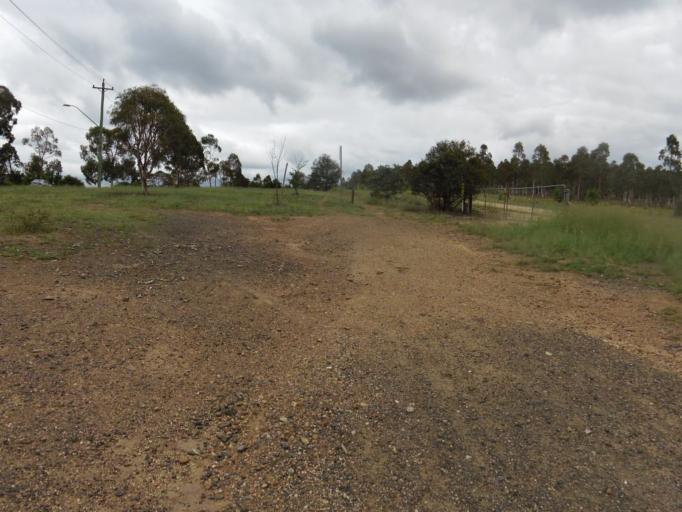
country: AU
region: Australian Capital Territory
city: Macquarie
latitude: -35.3324
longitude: 149.0267
